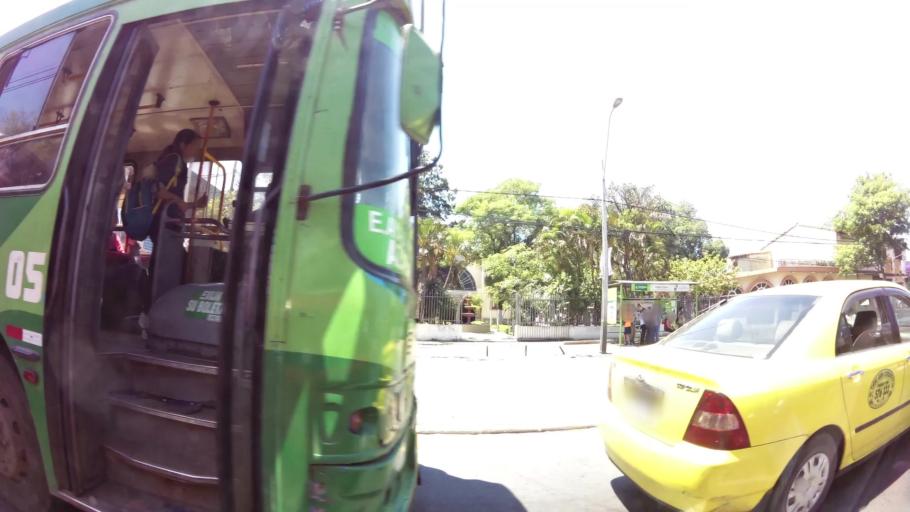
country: PY
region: Central
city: Fernando de la Mora
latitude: -25.3218
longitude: -57.5569
